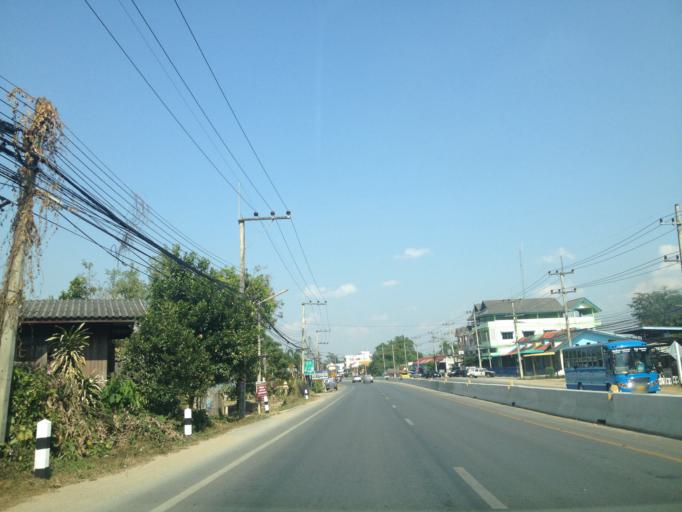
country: TH
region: Chiang Mai
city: San Pa Tong
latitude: 18.6087
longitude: 98.8936
